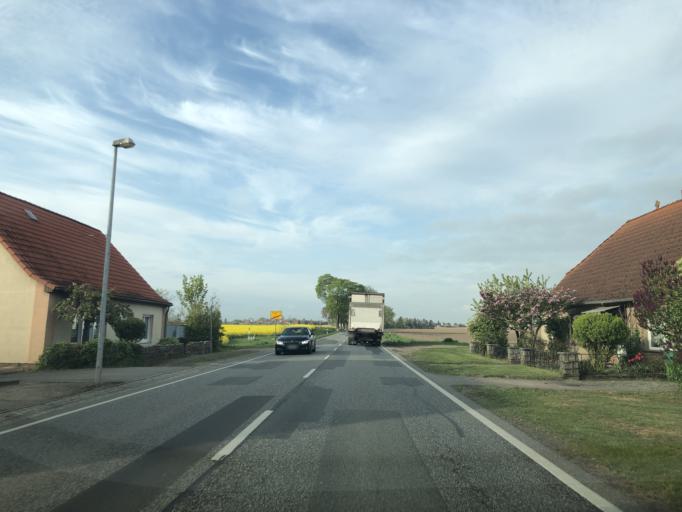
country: DE
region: Mecklenburg-Vorpommern
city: Guestrow
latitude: 53.8528
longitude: 12.2267
